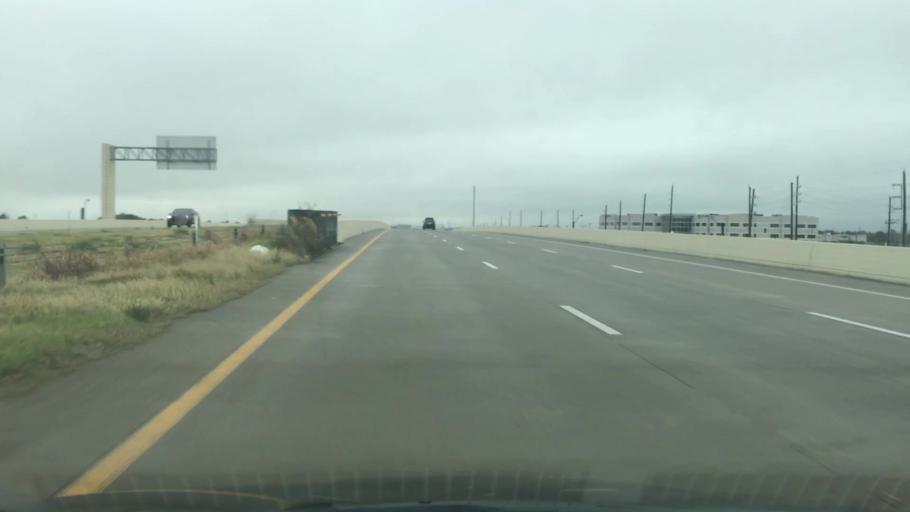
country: US
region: Texas
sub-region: Harris County
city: Katy
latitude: 29.8007
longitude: -95.7756
